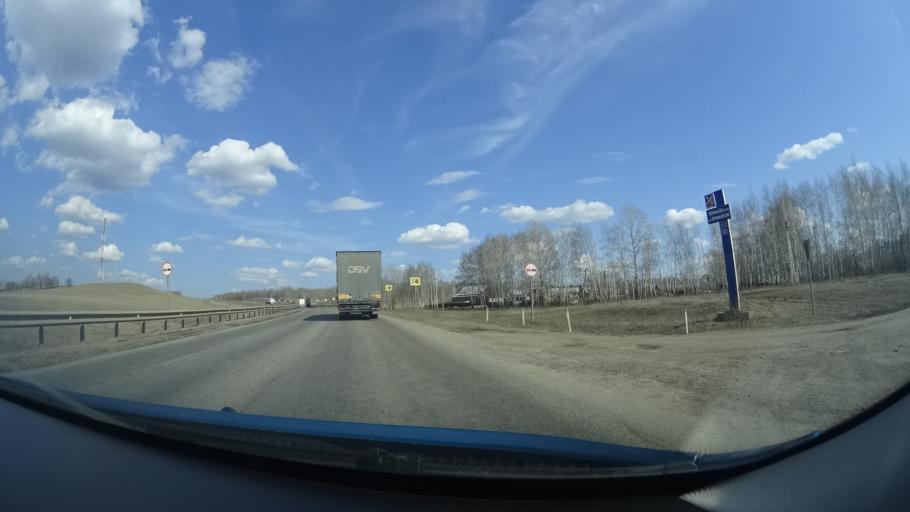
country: RU
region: Bashkortostan
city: Buzdyak
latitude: 54.6778
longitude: 54.7974
